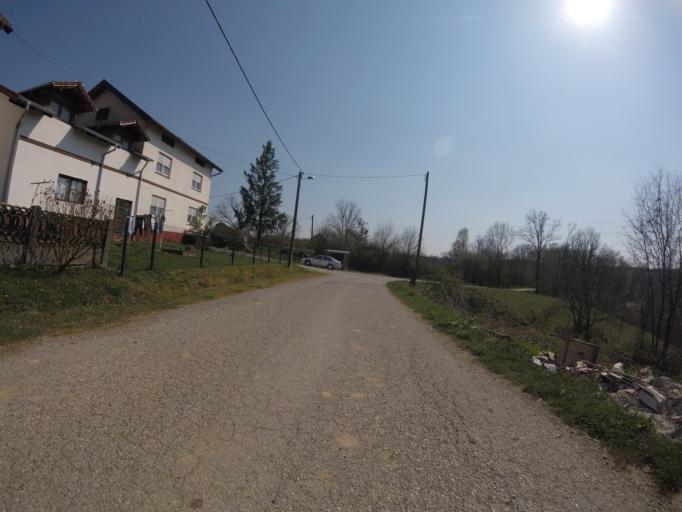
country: HR
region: Grad Zagreb
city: Strmec
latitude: 45.5880
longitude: 15.9230
